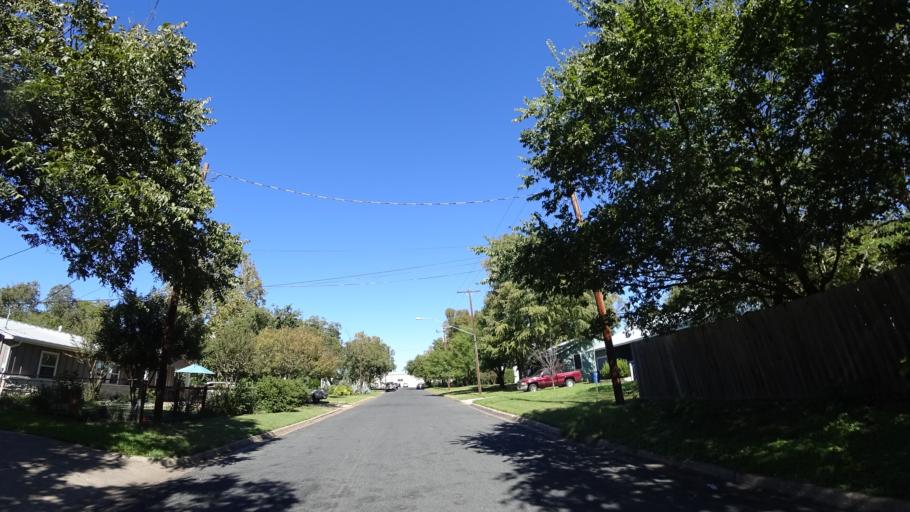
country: US
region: Texas
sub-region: Travis County
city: Rollingwood
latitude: 30.2249
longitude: -97.7845
